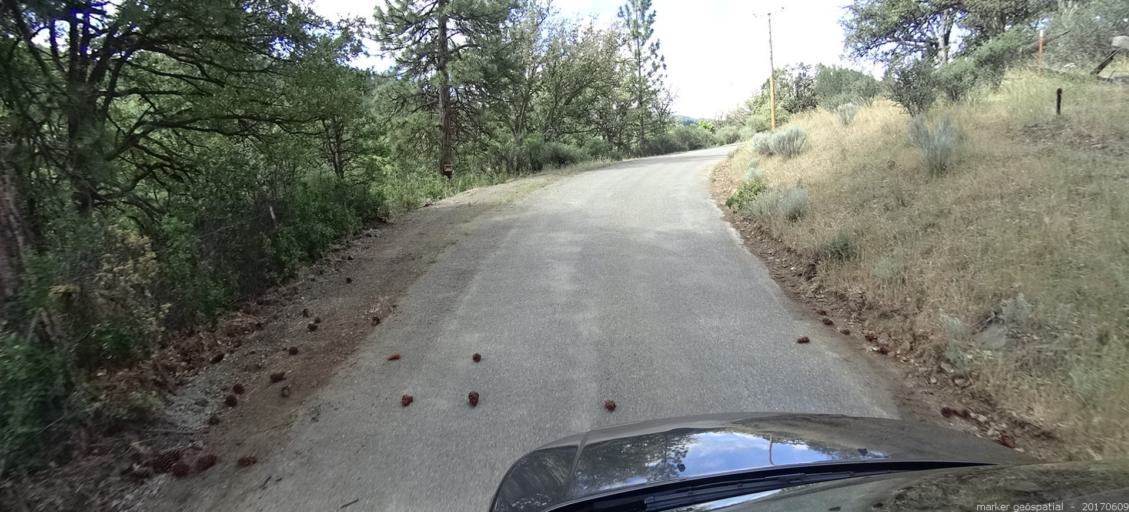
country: US
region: California
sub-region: Siskiyou County
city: Weed
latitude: 41.3154
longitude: -122.8179
